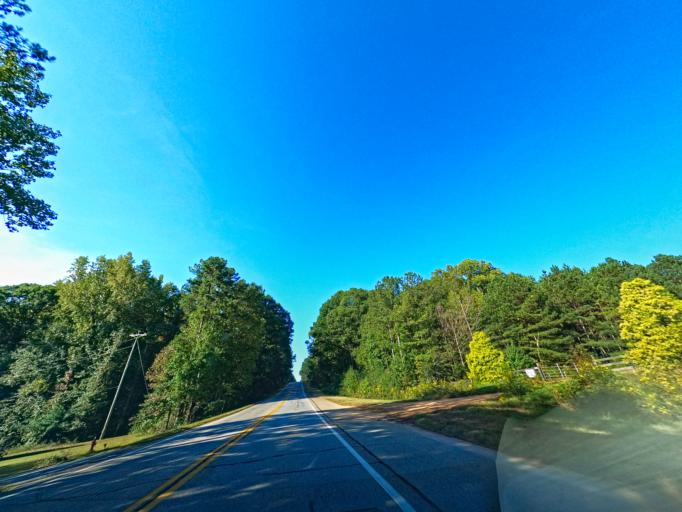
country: US
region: Georgia
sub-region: Coweta County
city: Newnan
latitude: 33.3649
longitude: -84.8922
